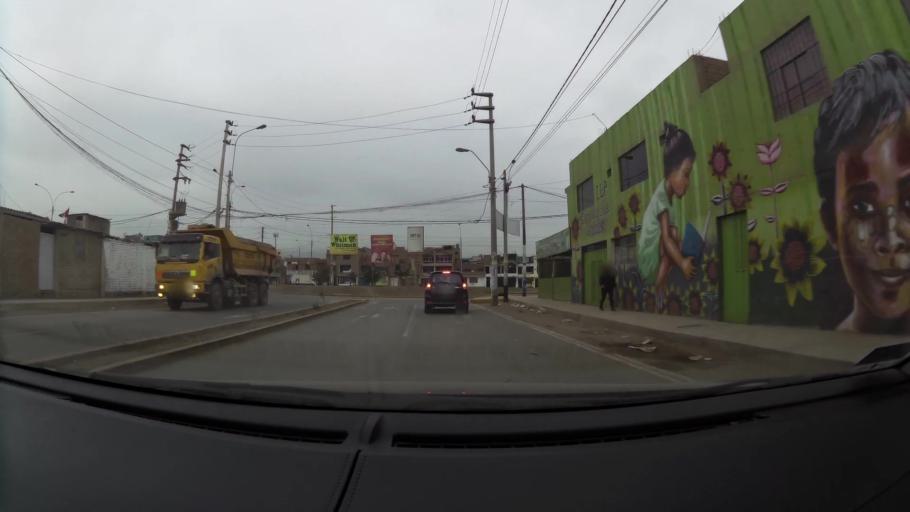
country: PE
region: Lima
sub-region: Lima
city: Independencia
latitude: -11.9709
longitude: -77.0859
